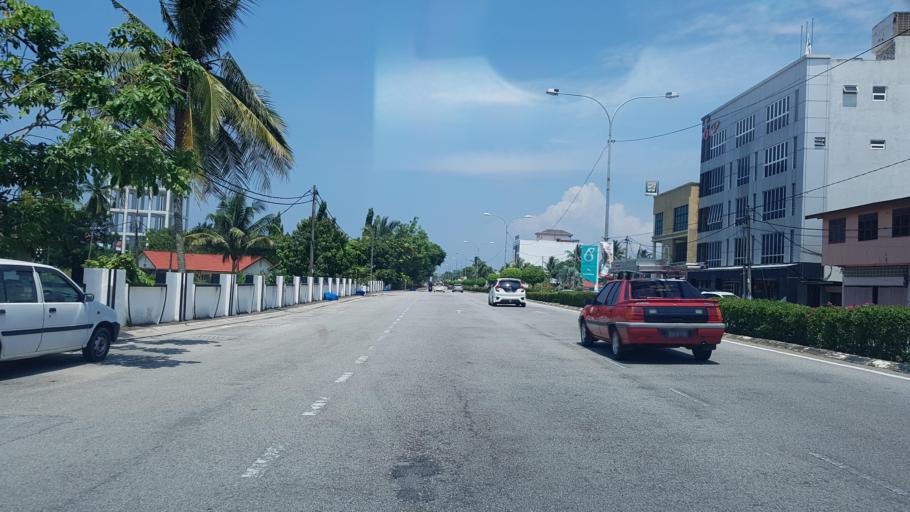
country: MY
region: Terengganu
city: Kuala Terengganu
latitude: 5.3131
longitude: 103.1555
